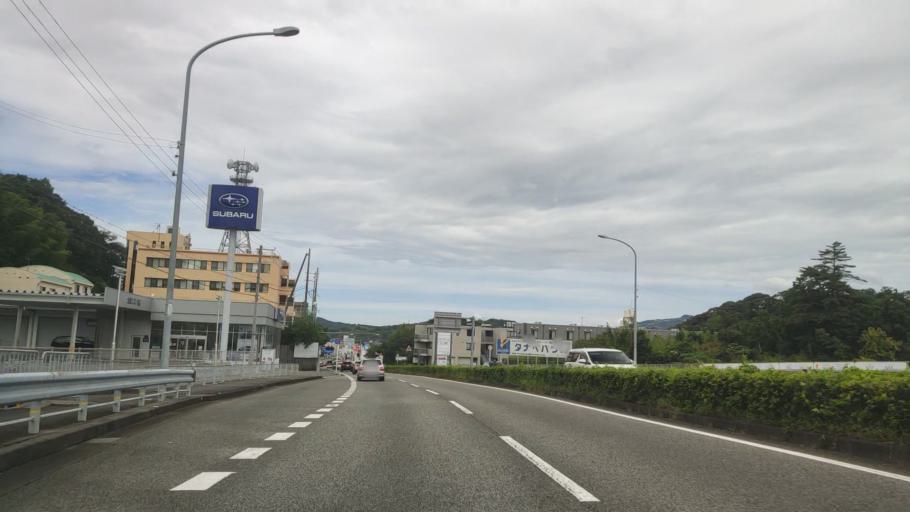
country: JP
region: Wakayama
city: Tanabe
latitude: 33.7355
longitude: 135.3997
